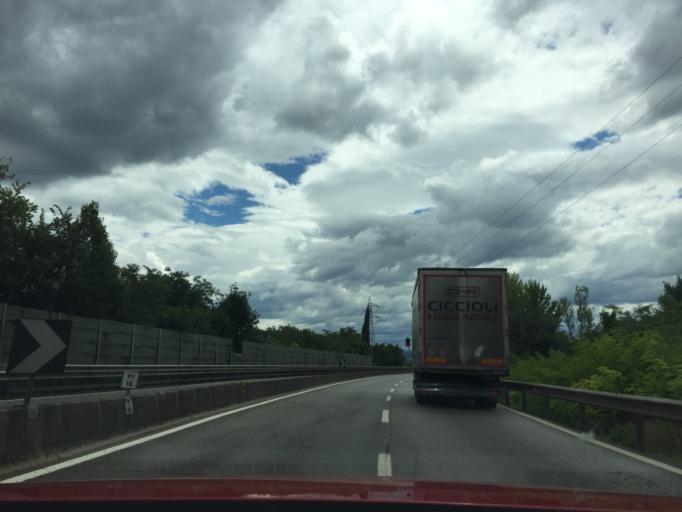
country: IT
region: Tuscany
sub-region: Province of Florence
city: Montelupo Fiorentino
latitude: 43.7249
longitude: 11.0198
